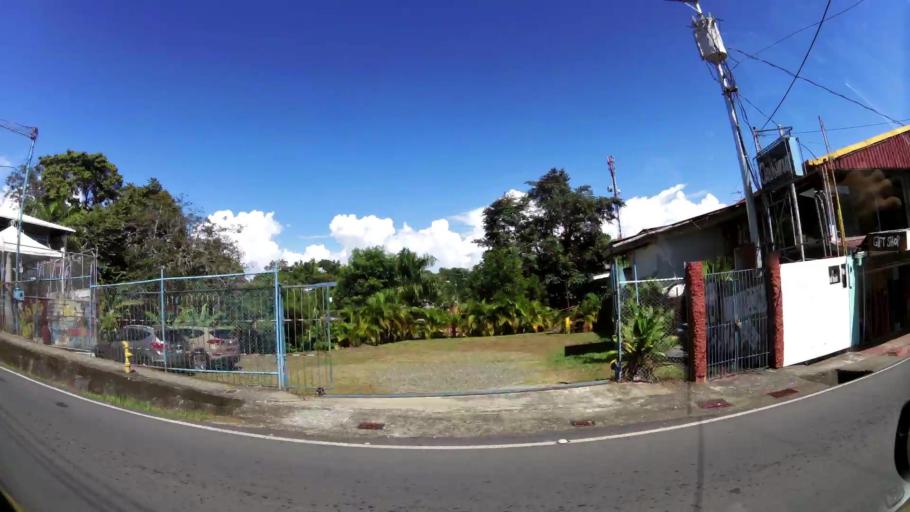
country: CR
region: Puntarenas
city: Quepos
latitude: 9.4064
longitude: -84.1576
